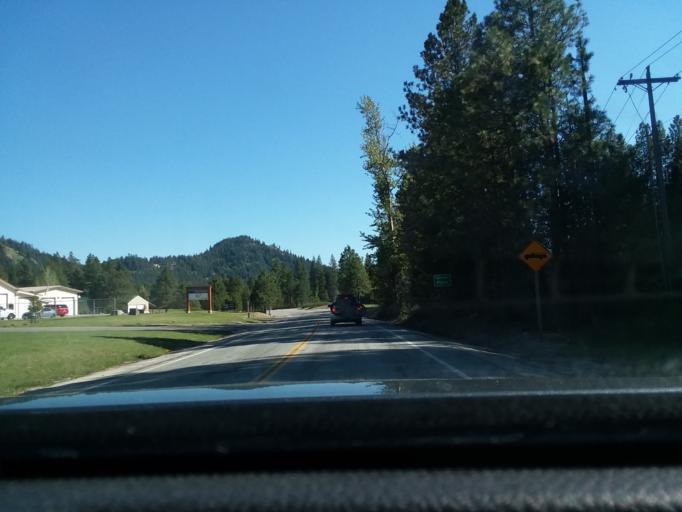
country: US
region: Washington
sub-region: Chelan County
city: Leavenworth
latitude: 47.7694
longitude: -120.6660
